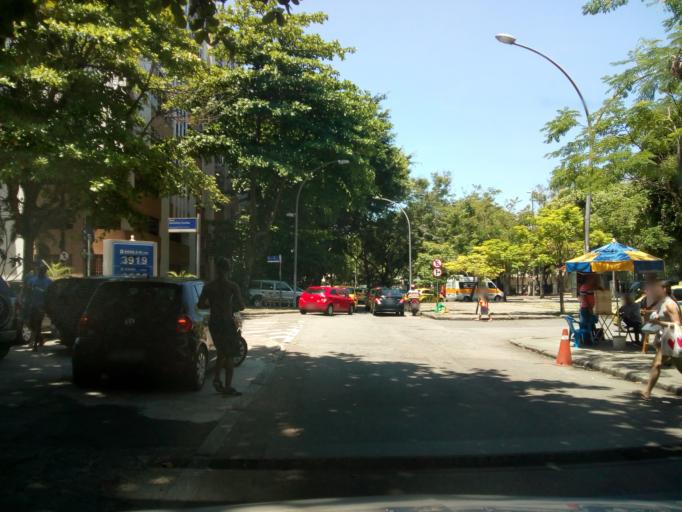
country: BR
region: Rio de Janeiro
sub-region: Rio De Janeiro
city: Rio de Janeiro
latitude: -22.9731
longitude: -43.2261
